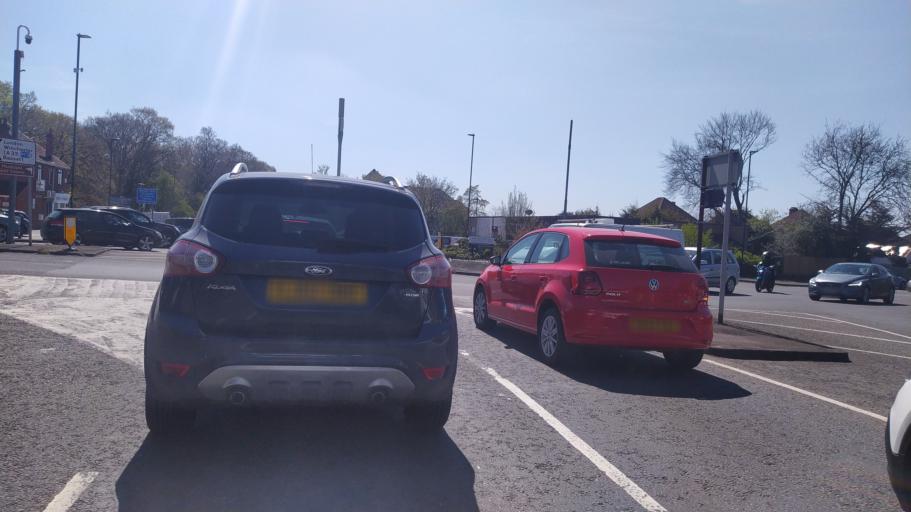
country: GB
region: England
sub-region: Southampton
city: Southampton
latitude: 50.9345
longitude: -1.4190
